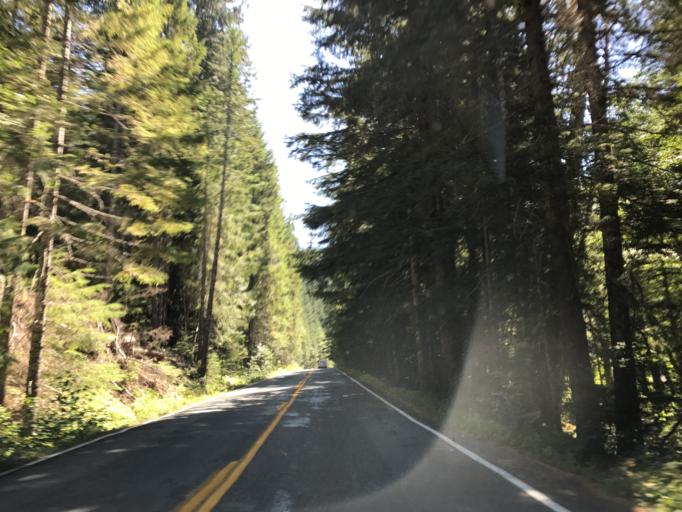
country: US
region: Washington
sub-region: Pierce County
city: Buckley
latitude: 46.7737
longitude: -121.5497
